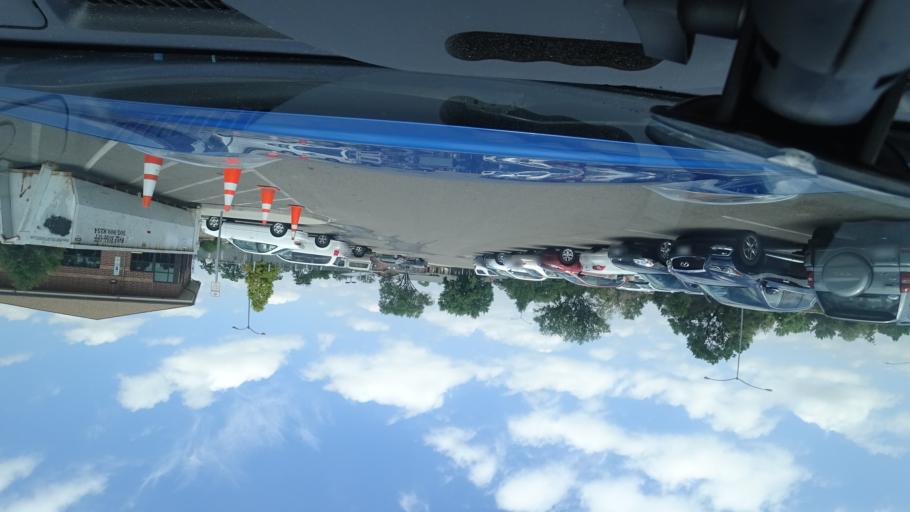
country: US
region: Colorado
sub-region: Adams County
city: Aurora
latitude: 39.7245
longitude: -104.8490
